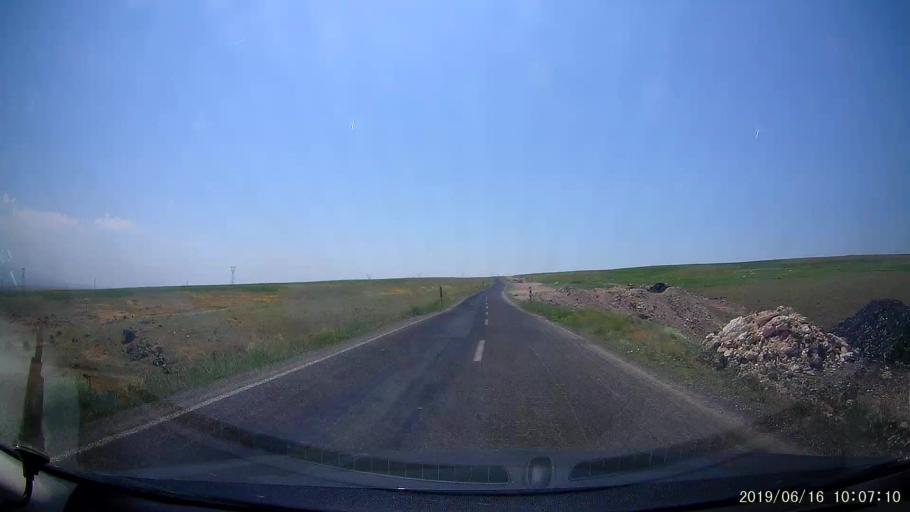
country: TR
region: Kars
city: Digor
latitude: 40.2473
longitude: 43.5521
